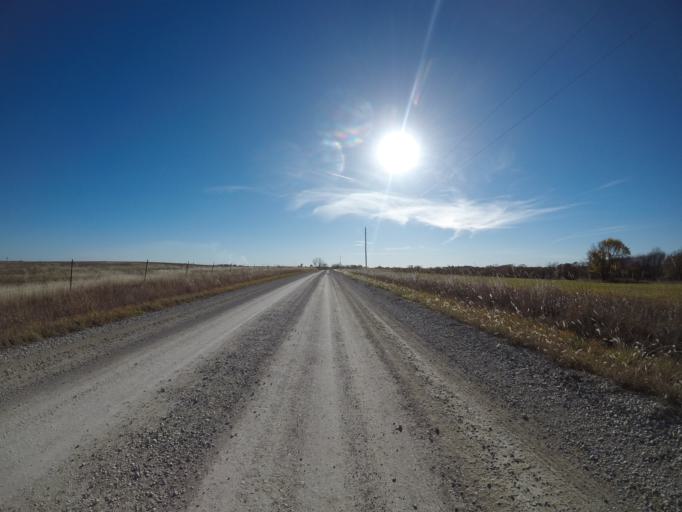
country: US
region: Kansas
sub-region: Riley County
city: Manhattan
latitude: 39.2794
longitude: -96.6794
